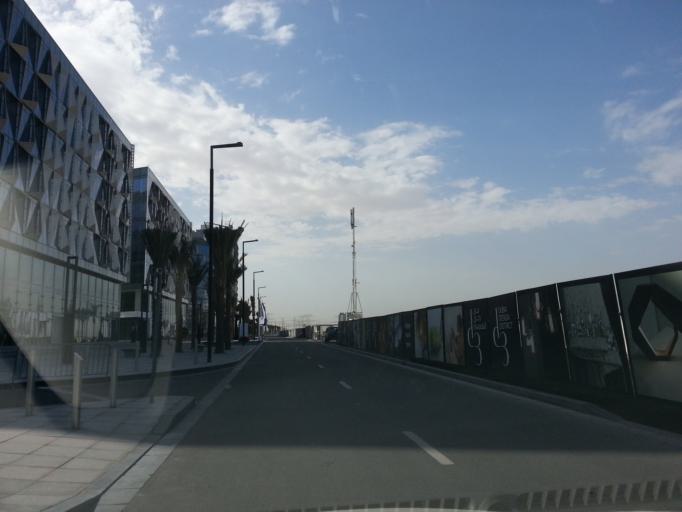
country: AE
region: Dubai
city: Dubai
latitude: 25.1898
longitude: 55.2965
